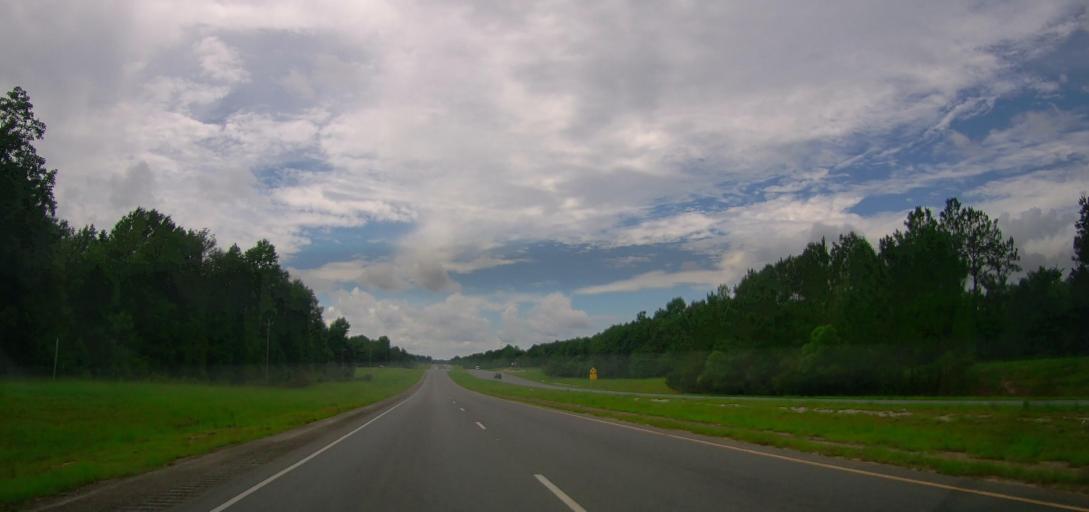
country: US
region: Georgia
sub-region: Telfair County
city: Helena
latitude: 32.1029
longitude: -83.0273
